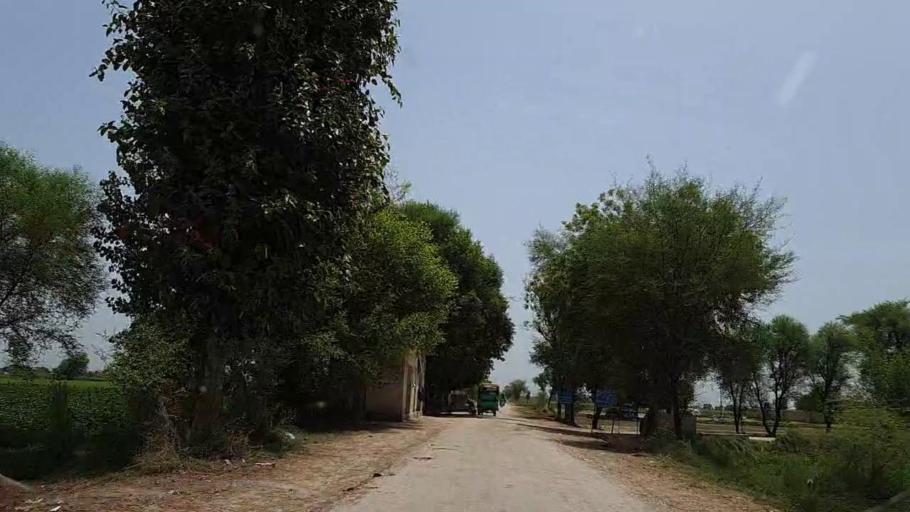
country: PK
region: Sindh
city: Tharu Shah
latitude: 26.9646
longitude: 68.0515
